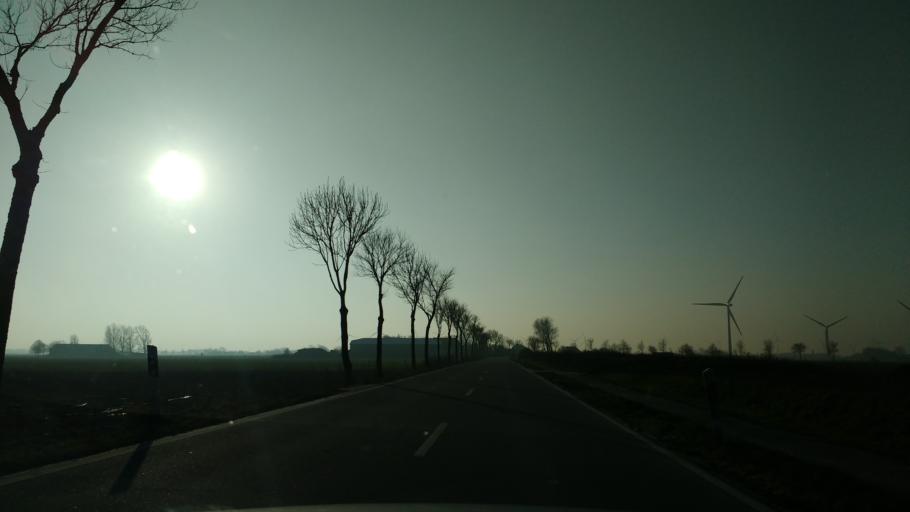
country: DE
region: Schleswig-Holstein
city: Helse
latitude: 53.9864
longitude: 8.9931
